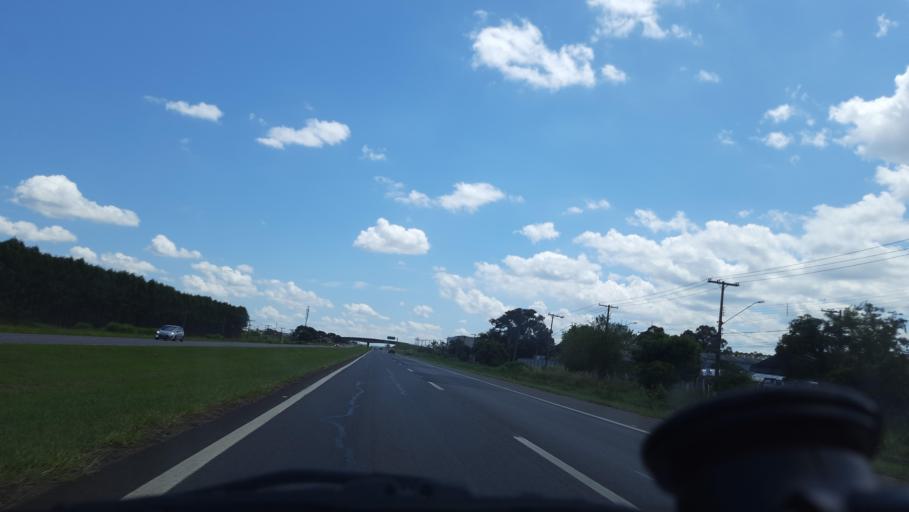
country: BR
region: Sao Paulo
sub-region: Moji-Guacu
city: Mogi-Gaucu
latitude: -22.3273
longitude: -46.9611
